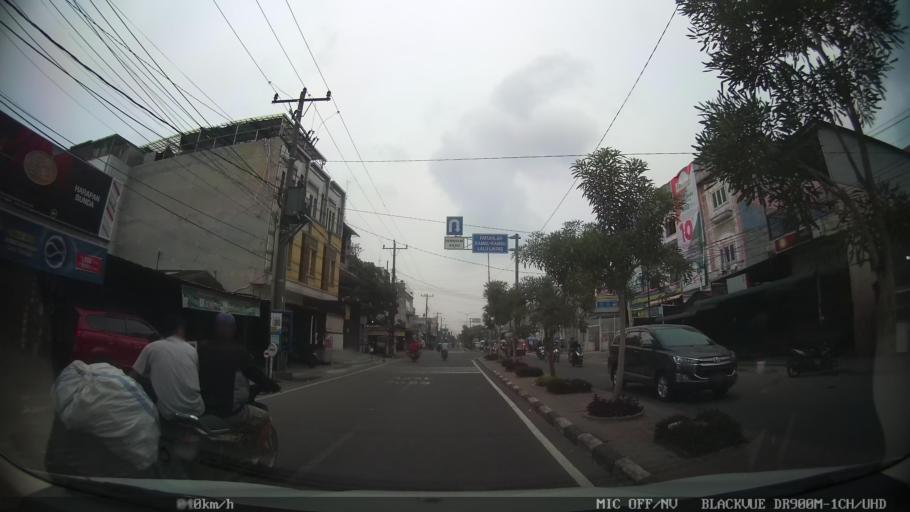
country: ID
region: North Sumatra
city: Medan
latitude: 3.5722
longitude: 98.7008
